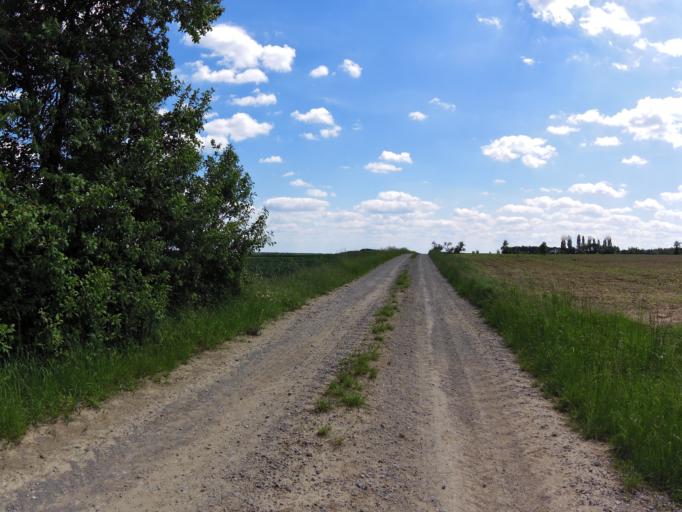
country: DE
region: Bavaria
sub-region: Regierungsbezirk Unterfranken
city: Biebelried
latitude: 49.7395
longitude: 10.0710
